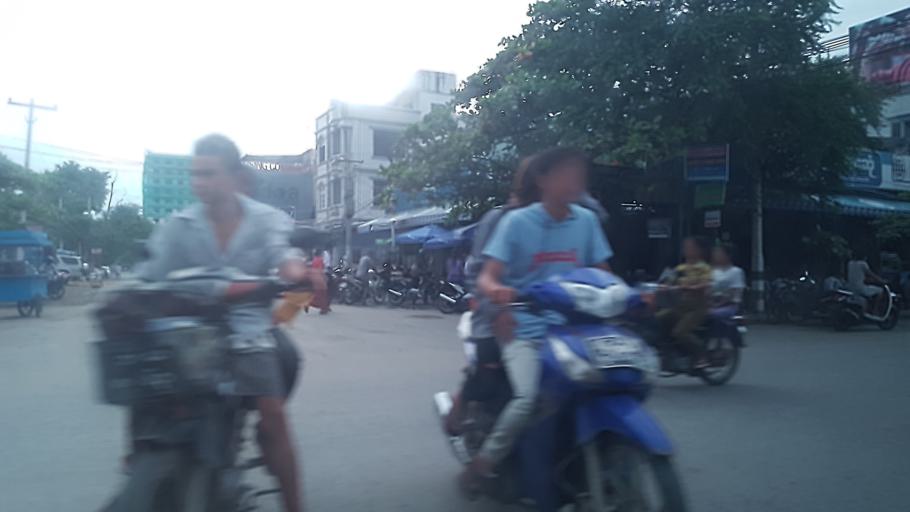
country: MM
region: Mandalay
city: Mandalay
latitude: 21.9672
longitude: 96.0950
